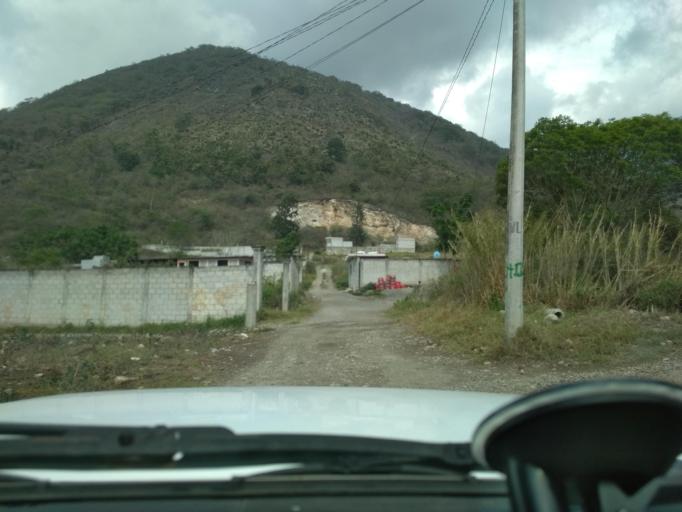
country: MX
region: Veracruz
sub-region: Nogales
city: Taza de Agua Ojo Zarco
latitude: 18.7851
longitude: -97.1979
